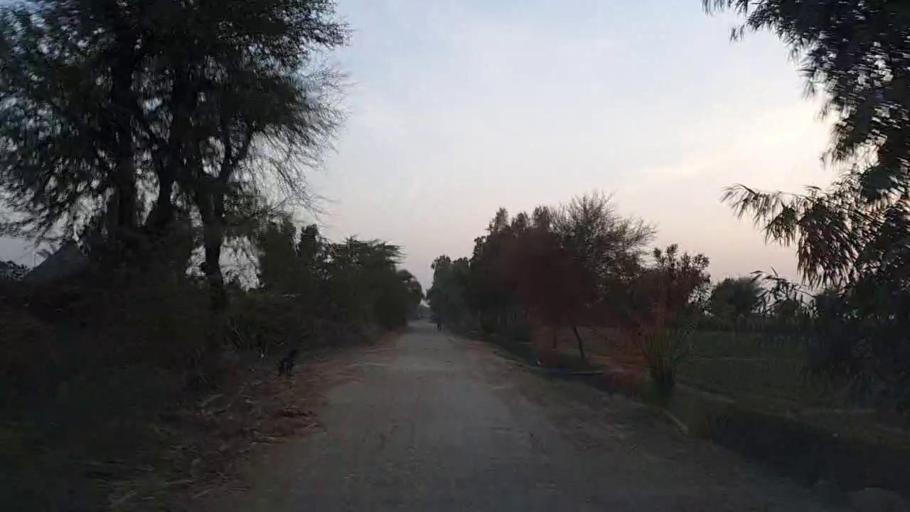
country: PK
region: Sindh
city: Tando Mittha Khan
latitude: 25.9445
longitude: 69.1546
